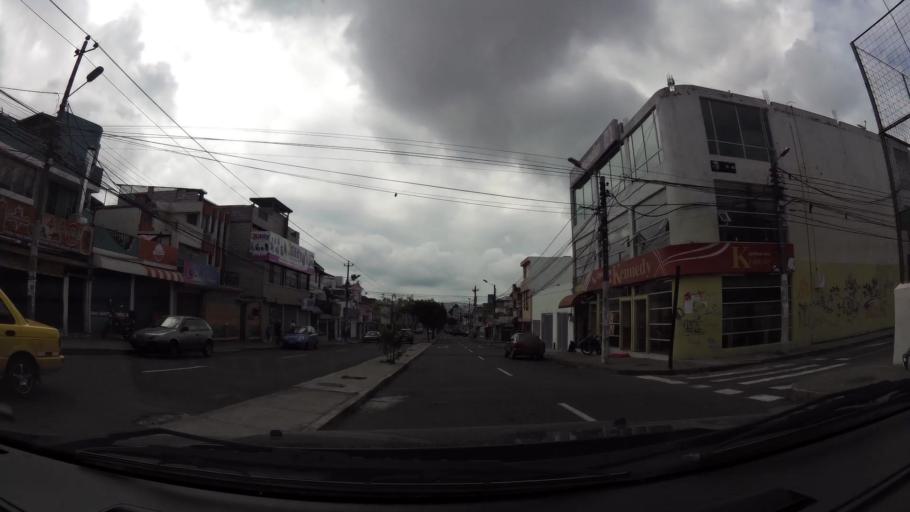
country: EC
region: Pichincha
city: Quito
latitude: -0.1432
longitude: -78.4944
